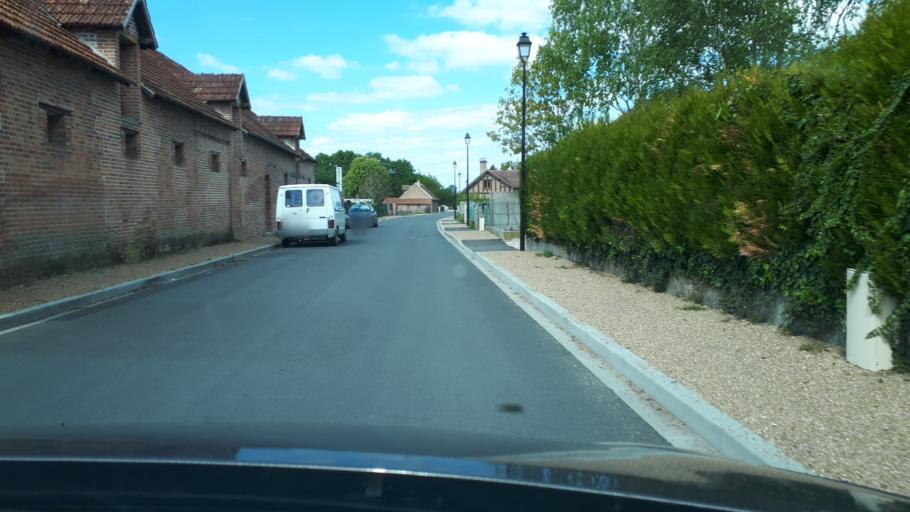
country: FR
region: Centre
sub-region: Departement du Loir-et-Cher
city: Saint-Viatre
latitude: 47.5224
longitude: 1.9319
